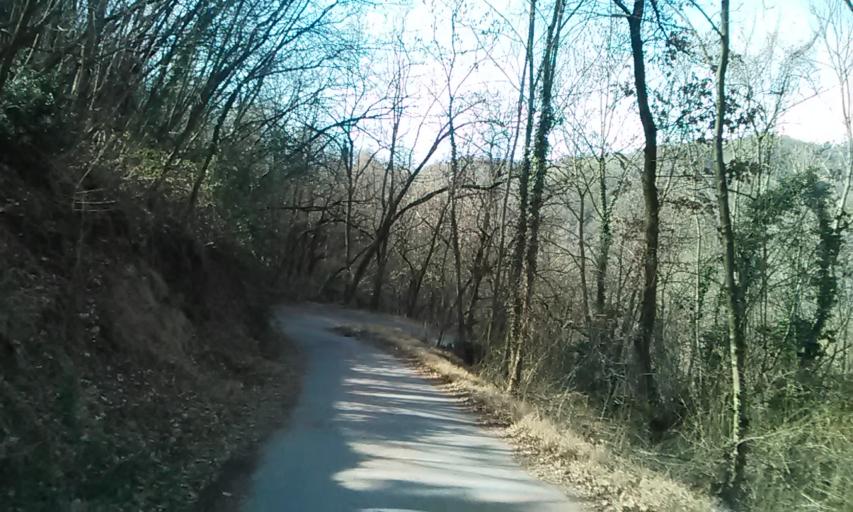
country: IT
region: Piedmont
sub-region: Provincia di Biella
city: Sostegno
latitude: 45.6544
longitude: 8.2593
